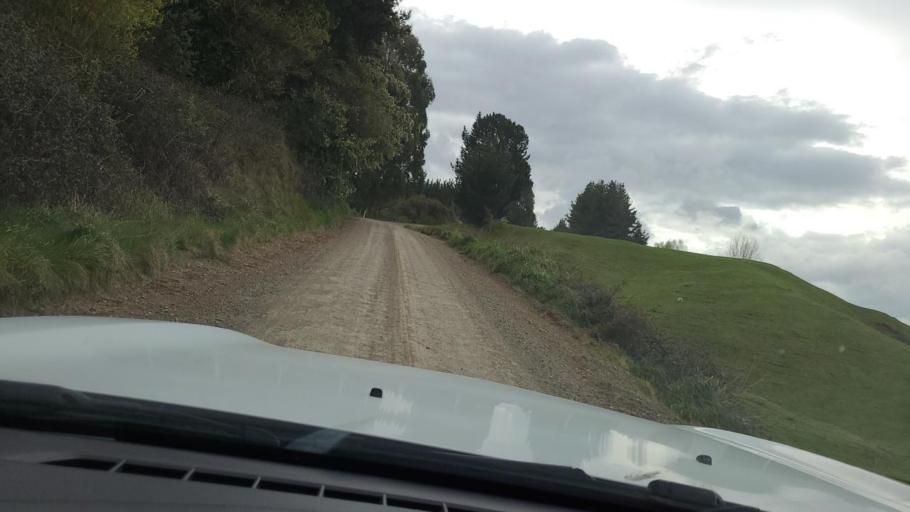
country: NZ
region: Hawke's Bay
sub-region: Napier City
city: Napier
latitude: -39.2613
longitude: 176.8424
